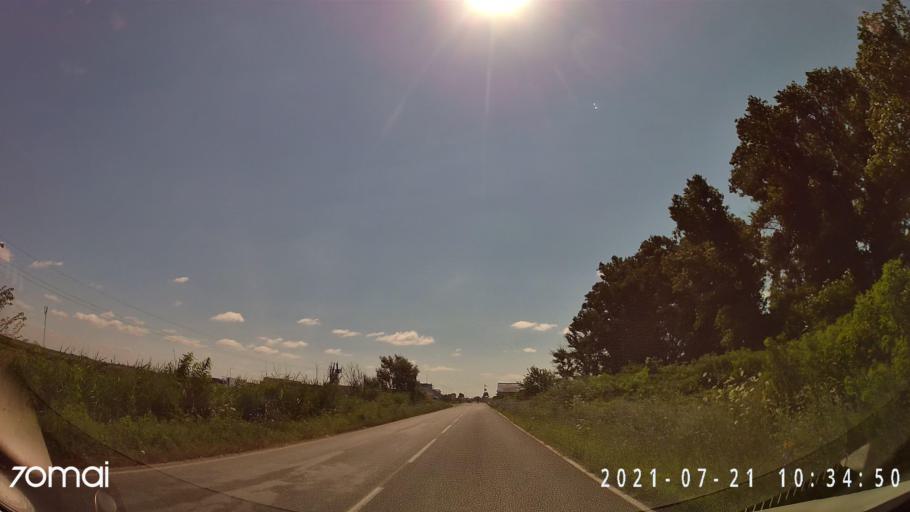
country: RO
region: Tulcea
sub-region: Oras Isaccea
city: Isaccea
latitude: 45.2934
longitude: 28.4542
